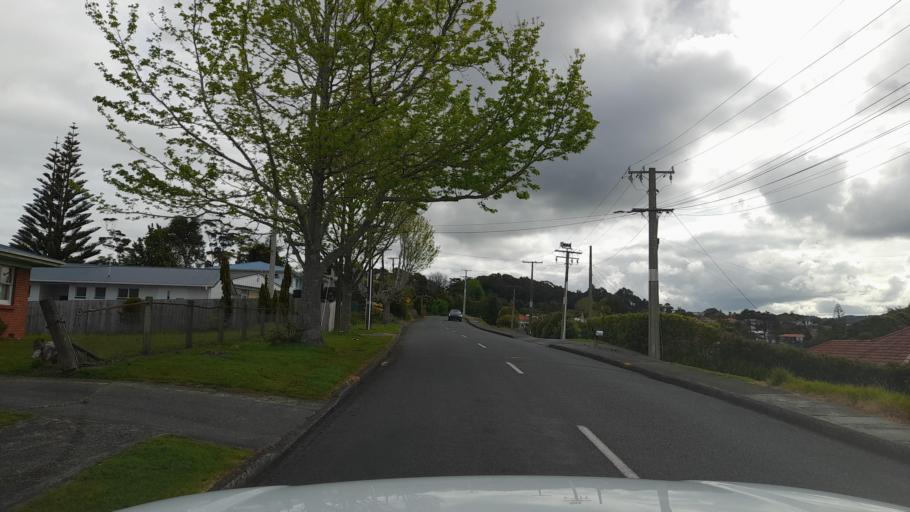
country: NZ
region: Northland
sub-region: Whangarei
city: Whangarei
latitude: -35.7384
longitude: 174.3231
